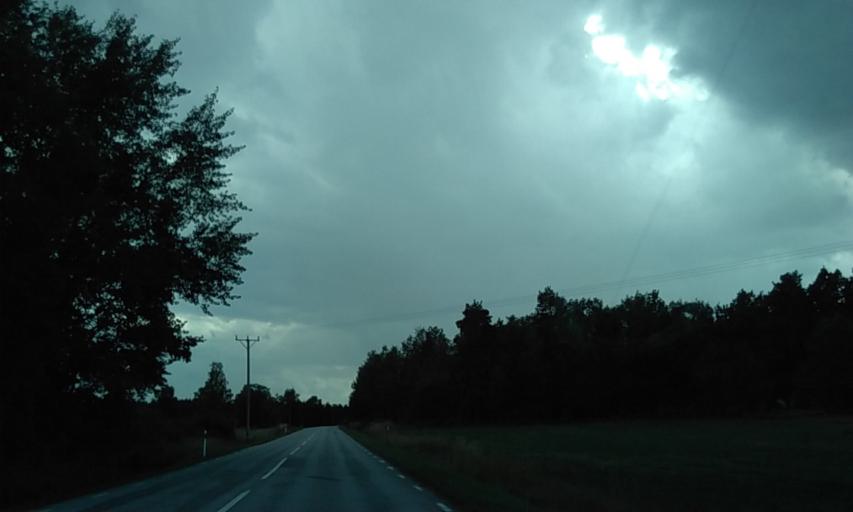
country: SE
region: Vaestra Goetaland
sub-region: Lidkopings Kommun
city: Lidkoping
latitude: 58.5041
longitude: 12.9867
